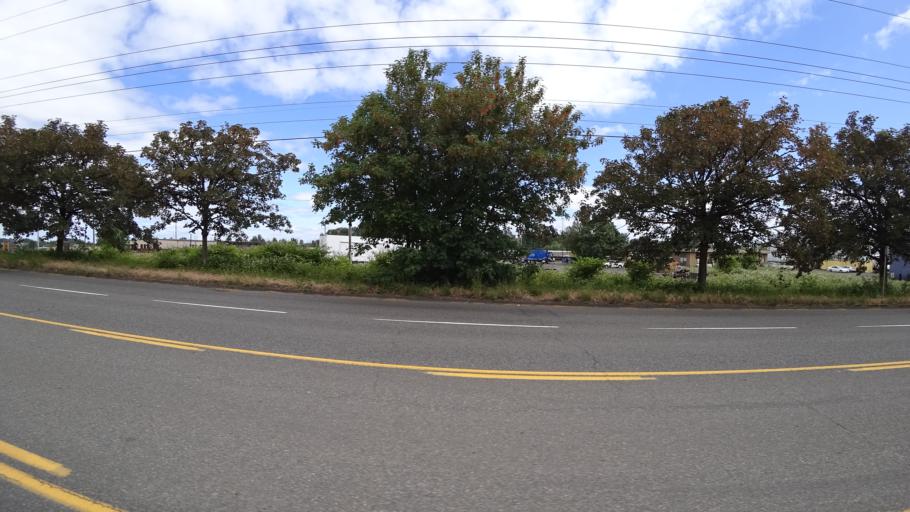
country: US
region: Oregon
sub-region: Washington County
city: West Haven
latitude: 45.6048
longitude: -122.7522
